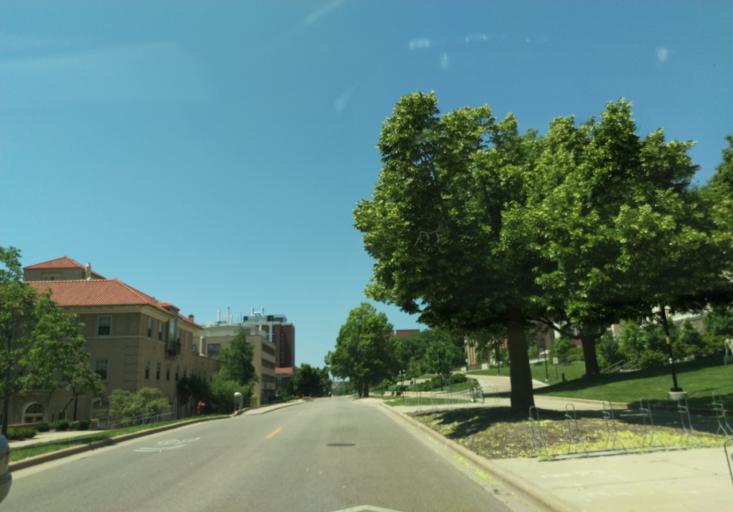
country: US
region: Wisconsin
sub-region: Dane County
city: Madison
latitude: 43.0752
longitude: -89.4081
